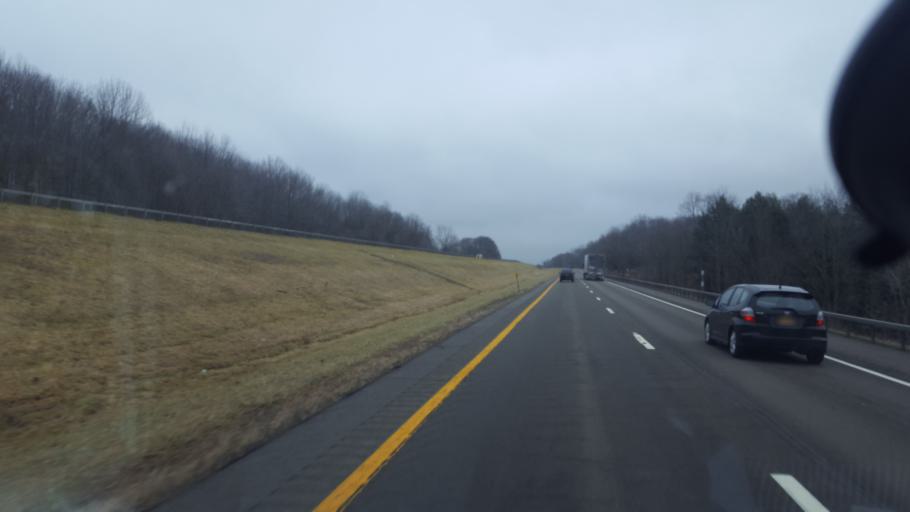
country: US
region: New York
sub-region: Cattaraugus County
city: Randolph
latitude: 42.1470
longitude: -79.0752
